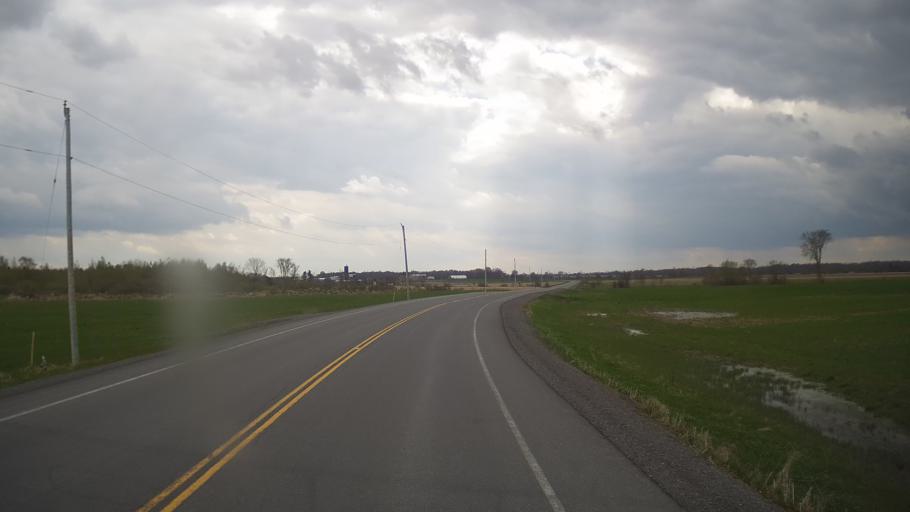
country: CA
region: Ontario
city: Hawkesbury
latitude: 45.5577
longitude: -74.5355
